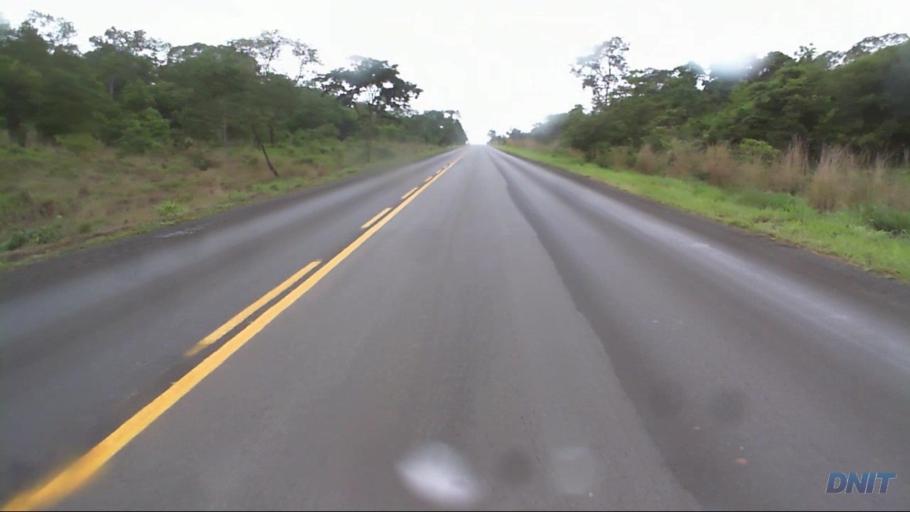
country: BR
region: Goias
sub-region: Padre Bernardo
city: Padre Bernardo
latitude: -15.2051
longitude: -48.4622
